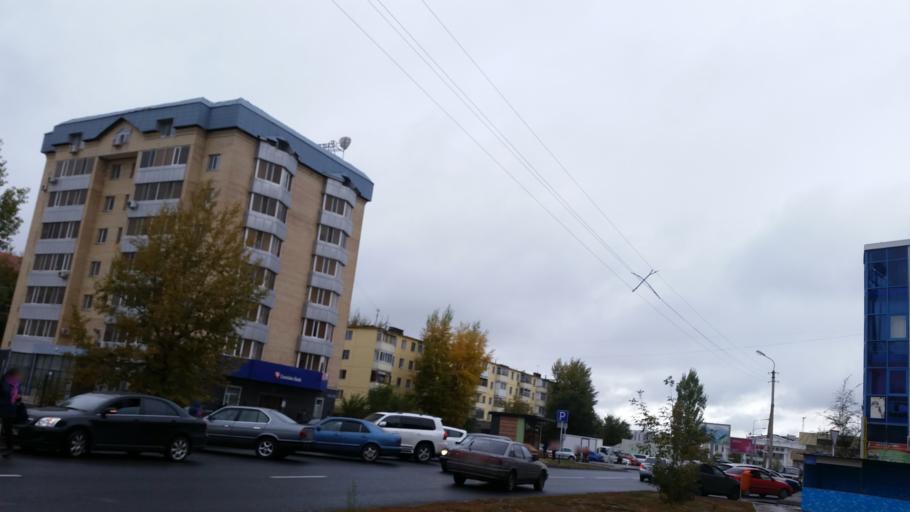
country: KZ
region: Astana Qalasy
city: Astana
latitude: 51.1507
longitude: 71.4625
